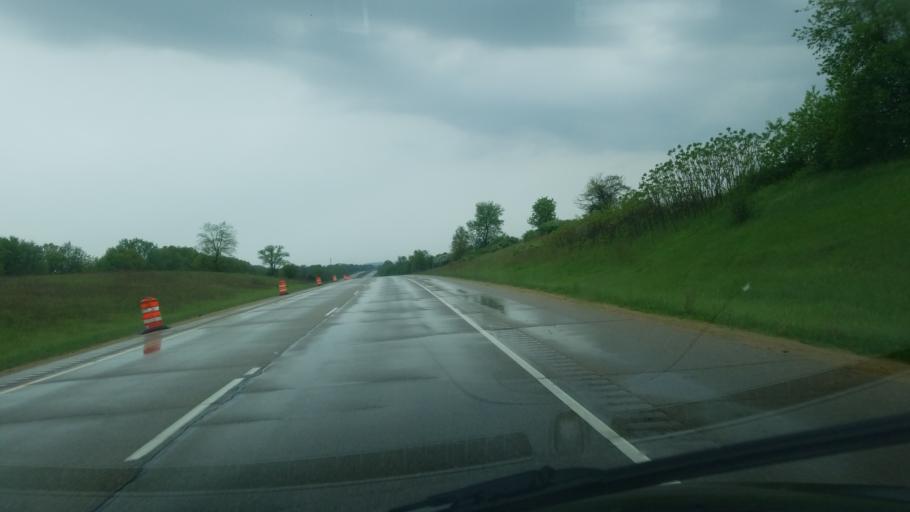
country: US
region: Wisconsin
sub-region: Dane County
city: Oregon
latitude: 42.9762
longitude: -89.3856
